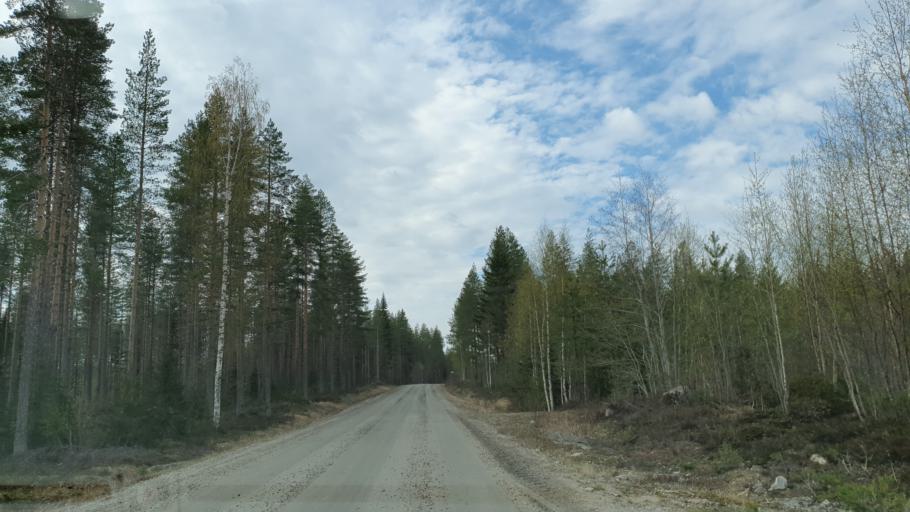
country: FI
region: Kainuu
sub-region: Kehys-Kainuu
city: Kuhmo
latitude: 64.0977
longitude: 29.9274
